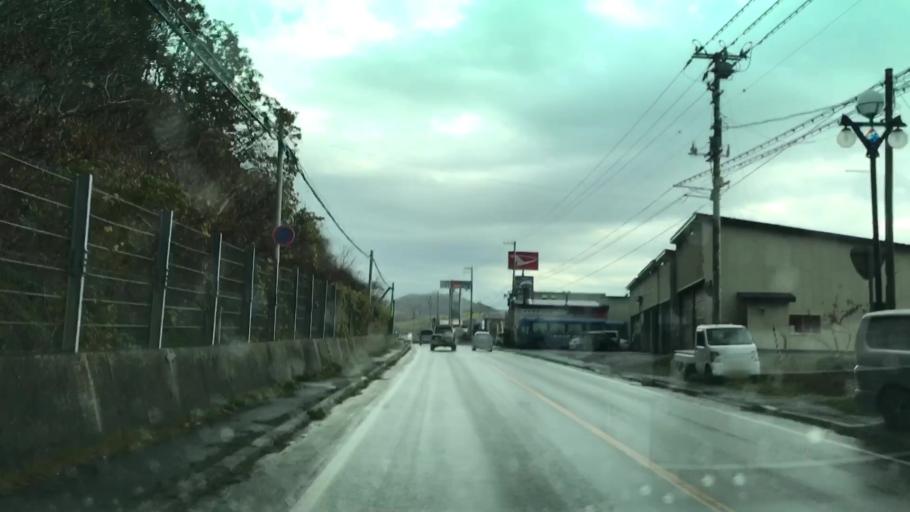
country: JP
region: Hokkaido
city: Shizunai-furukawacho
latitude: 42.1769
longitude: 142.7527
